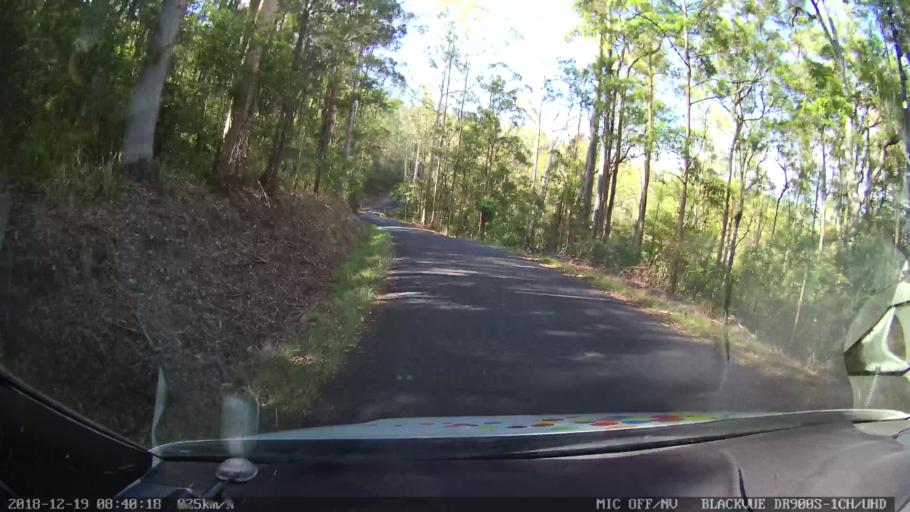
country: AU
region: New South Wales
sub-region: Kyogle
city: Kyogle
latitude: -28.3387
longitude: 152.9692
